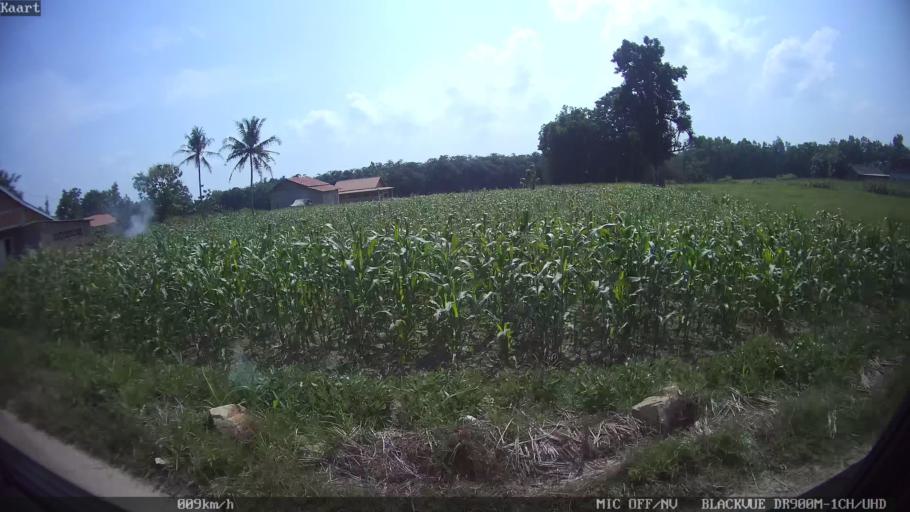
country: ID
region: Lampung
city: Natar
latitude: -5.2575
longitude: 105.1969
